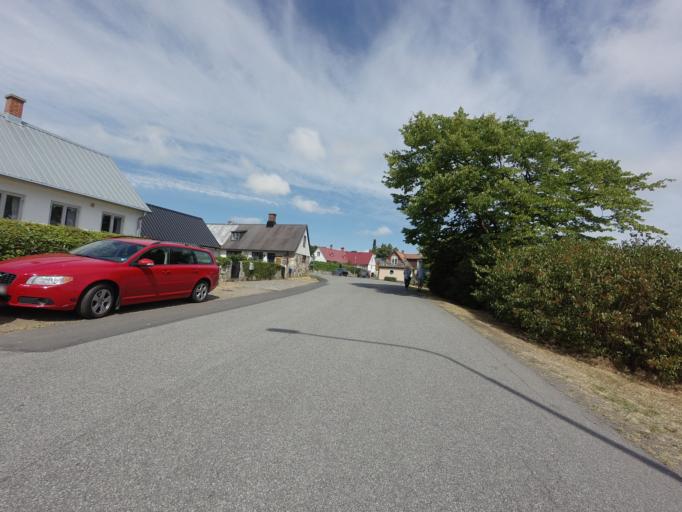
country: SE
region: Skane
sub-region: Simrishamns Kommun
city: Simrishamn
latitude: 55.5173
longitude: 14.3467
